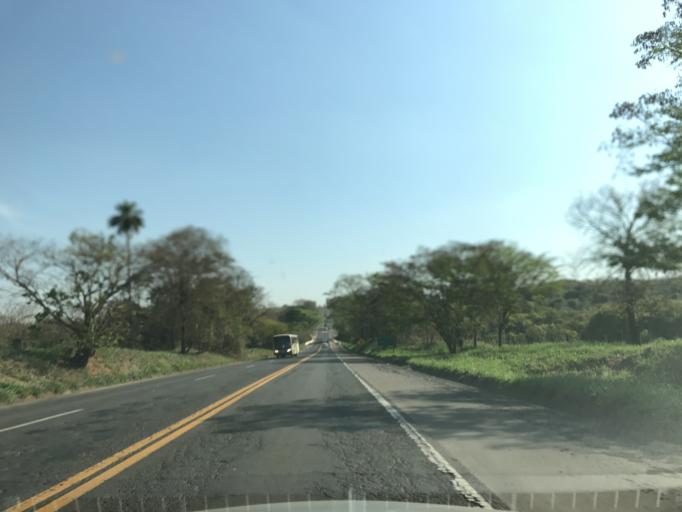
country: BR
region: Sao Paulo
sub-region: Penapolis
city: Penapolis
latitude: -21.4574
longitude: -50.1697
